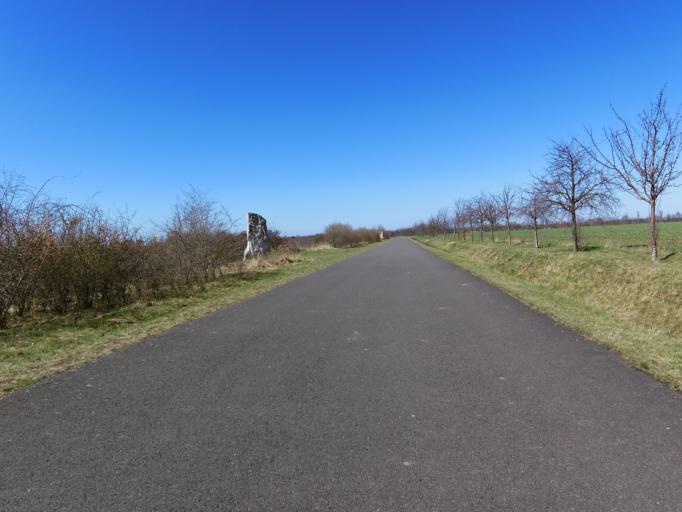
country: DE
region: Saxony
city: Markkleeberg
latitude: 51.2666
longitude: 12.4209
